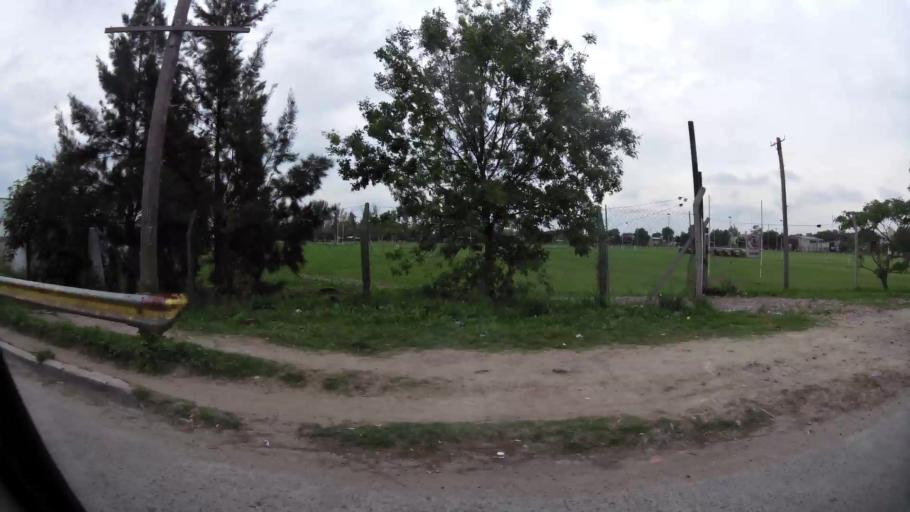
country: AR
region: Buenos Aires
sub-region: Partido de La Plata
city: La Plata
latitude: -34.9097
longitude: -57.9976
